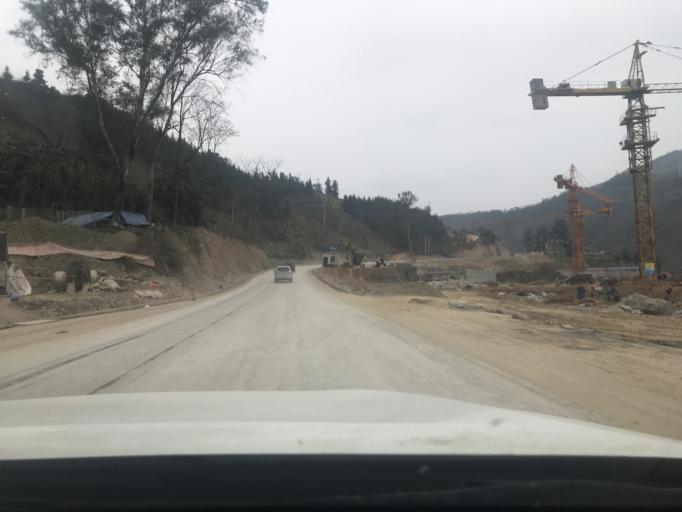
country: CN
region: Guangxi Zhuangzu Zizhiqu
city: Xinzhou
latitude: 25.0091
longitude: 105.8523
